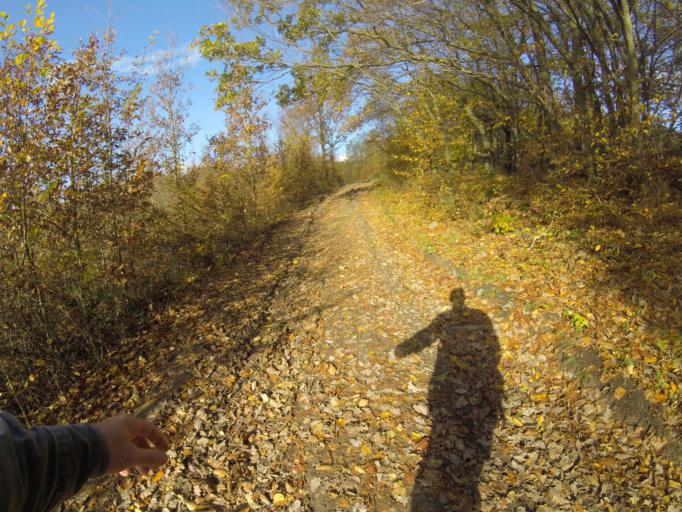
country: HU
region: Borsod-Abauj-Zemplen
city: Tolcsva
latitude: 48.3807
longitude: 21.3894
